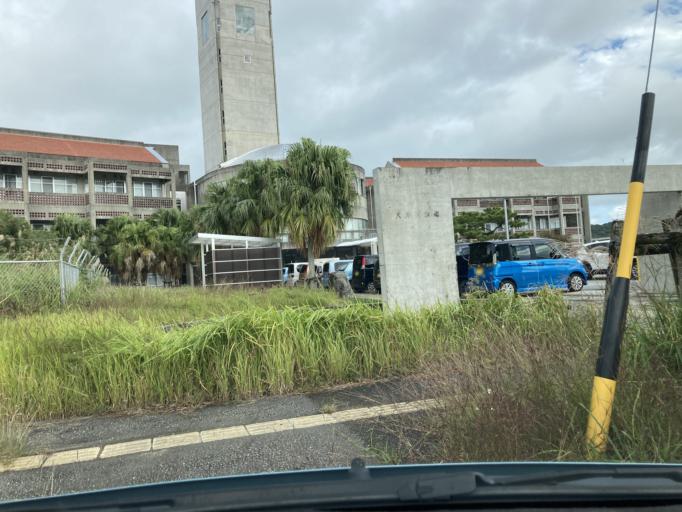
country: JP
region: Okinawa
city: Tomigusuku
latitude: 26.1758
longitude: 127.7439
